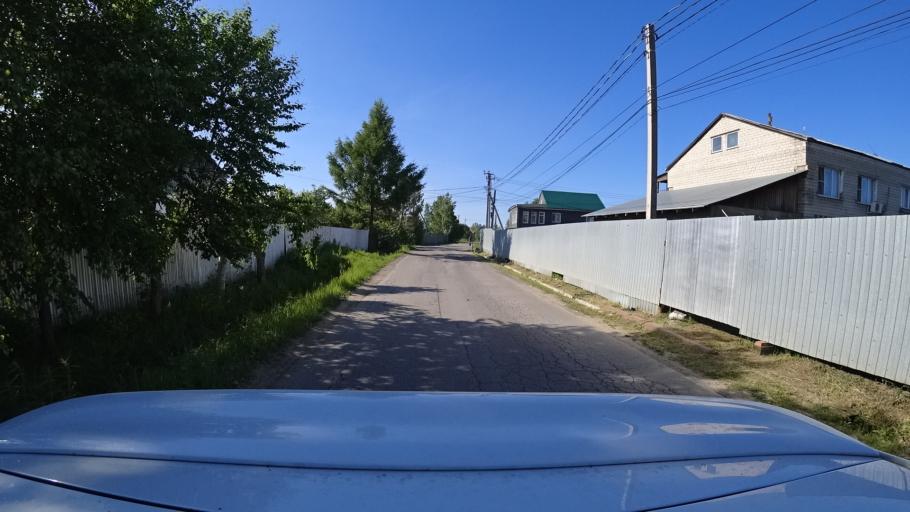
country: RU
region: Khabarovsk Krai
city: Topolevo
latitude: 48.5432
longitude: 135.1739
